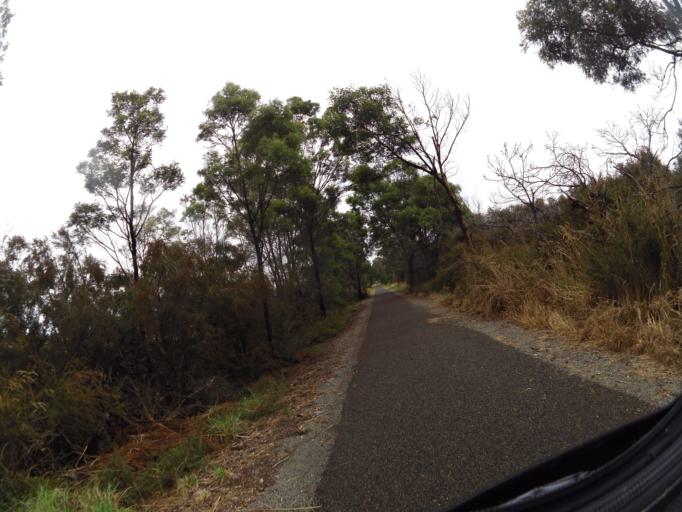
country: AU
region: Victoria
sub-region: East Gippsland
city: Bairnsdale
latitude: -37.8218
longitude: 147.7124
